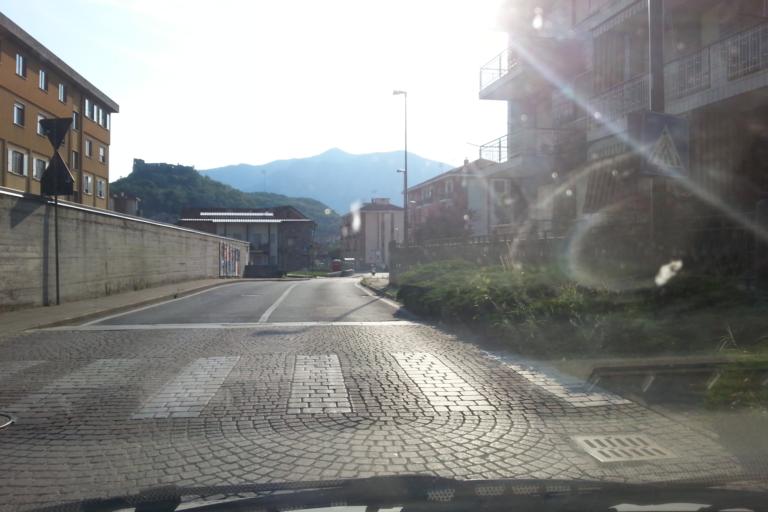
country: IT
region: Piedmont
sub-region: Provincia di Torino
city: Avigliana
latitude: 45.0829
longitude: 7.4042
